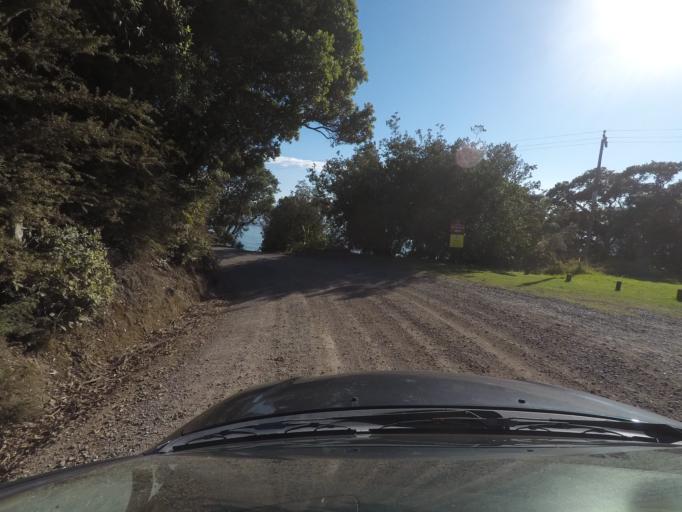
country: NZ
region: Northland
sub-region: Far North District
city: Paihia
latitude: -35.2544
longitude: 174.0720
